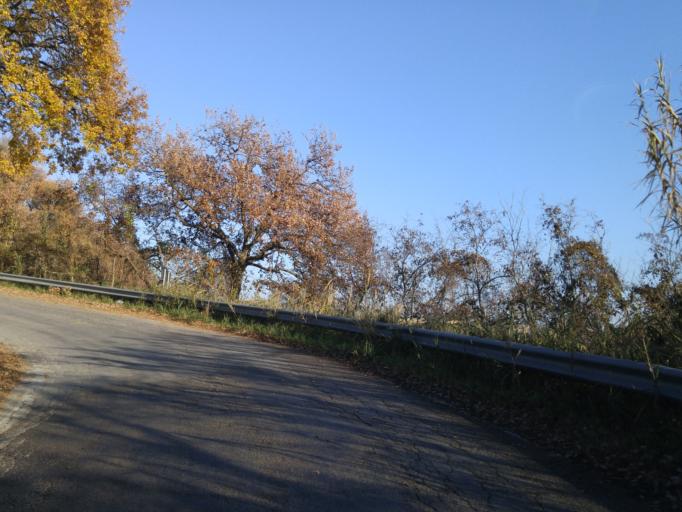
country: IT
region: The Marches
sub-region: Provincia di Pesaro e Urbino
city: Montefelcino
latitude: 43.7247
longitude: 12.8434
